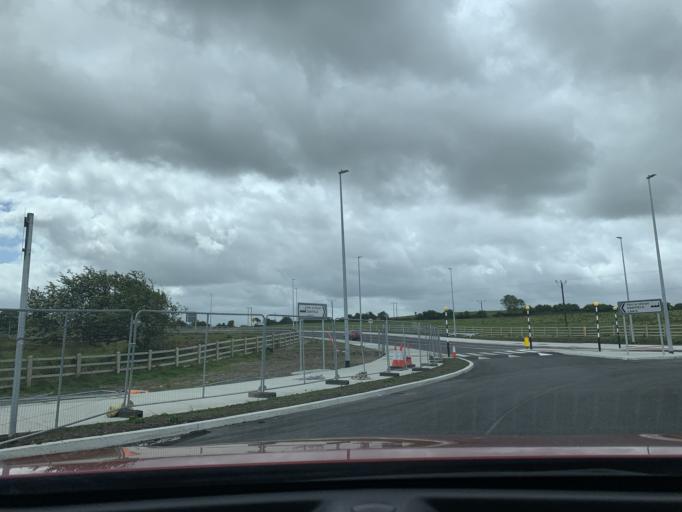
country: IE
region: Connaught
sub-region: Sligo
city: Sligo
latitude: 54.2602
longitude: -8.4961
